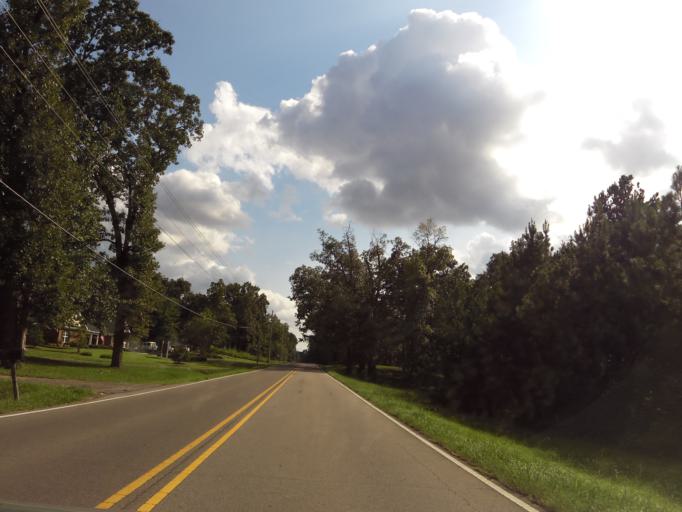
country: US
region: Mississippi
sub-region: Alcorn County
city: Corinth
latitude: 34.9596
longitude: -88.5173
